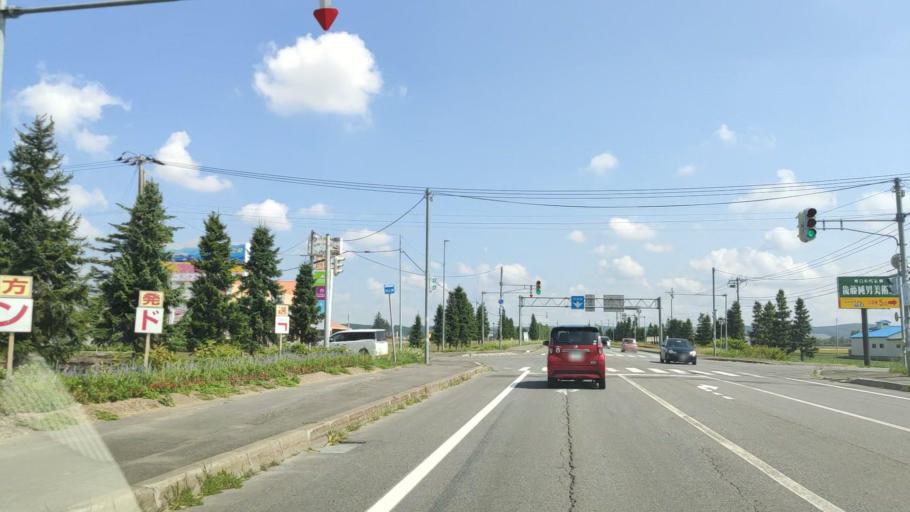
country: JP
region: Hokkaido
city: Shimo-furano
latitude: 43.4753
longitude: 142.4558
